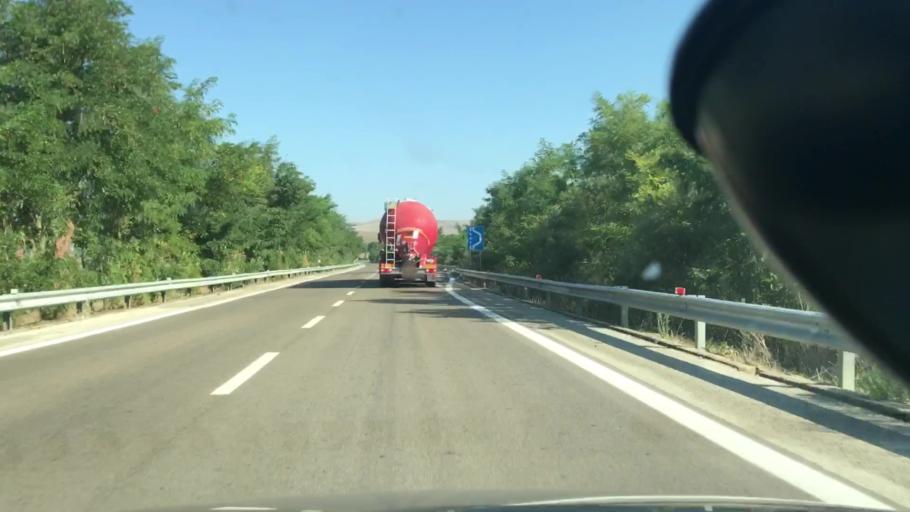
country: IT
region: Basilicate
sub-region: Provincia di Matera
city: Irsina
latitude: 40.8017
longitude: 16.2743
